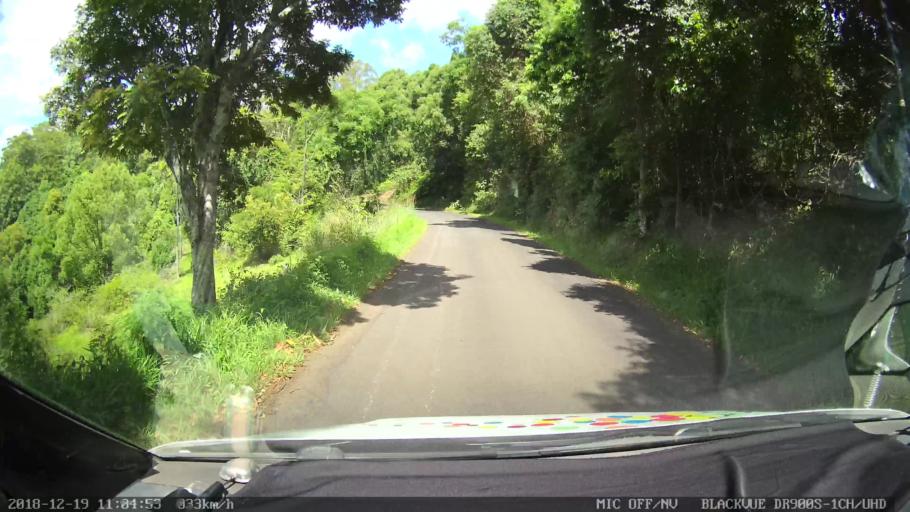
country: AU
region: New South Wales
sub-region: Lismore Municipality
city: Nimbin
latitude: -28.6154
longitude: 153.2661
